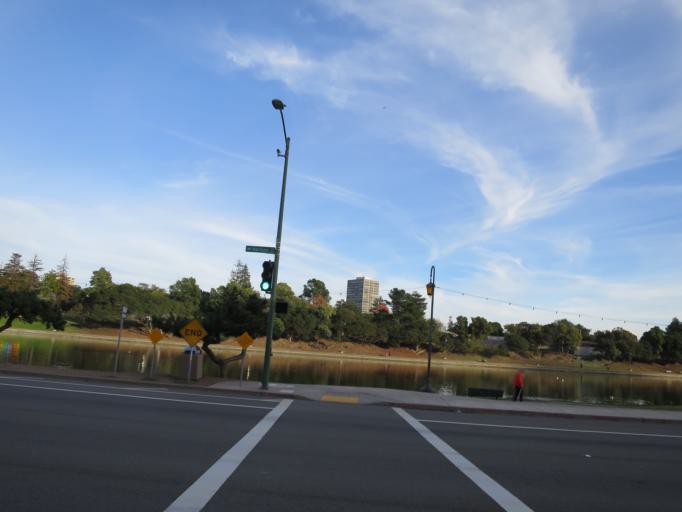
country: US
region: California
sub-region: Alameda County
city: Oakland
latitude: 37.8092
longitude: -122.2629
